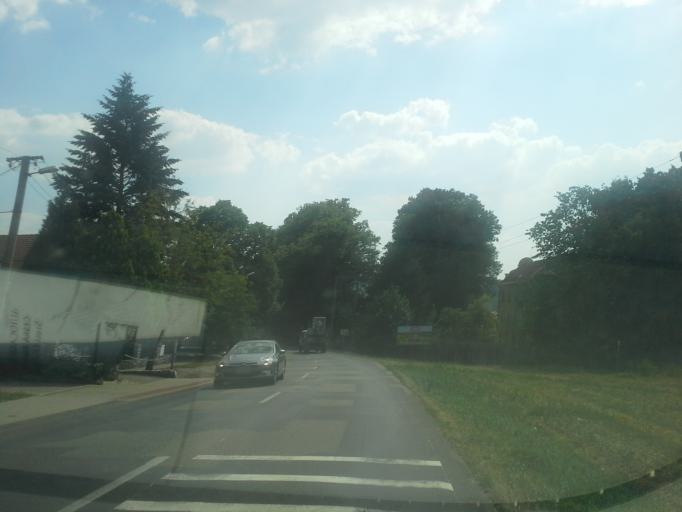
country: CZ
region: South Moravian
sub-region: Okres Blansko
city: Boskovice
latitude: 49.4957
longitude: 16.6632
